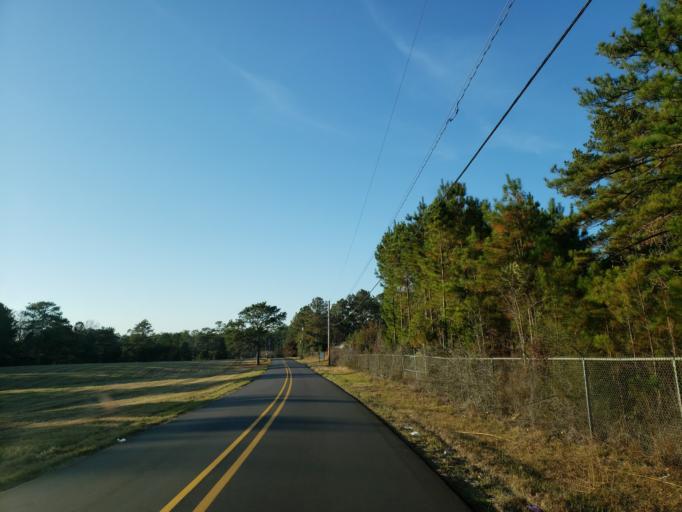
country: US
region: Mississippi
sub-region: Lamar County
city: Arnold Line
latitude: 31.3526
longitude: -89.3590
